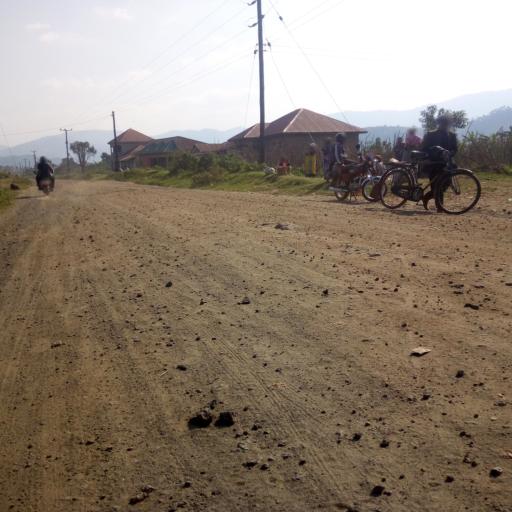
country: UG
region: Western Region
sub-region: Kisoro District
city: Kisoro
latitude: -1.2427
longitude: 29.7138
